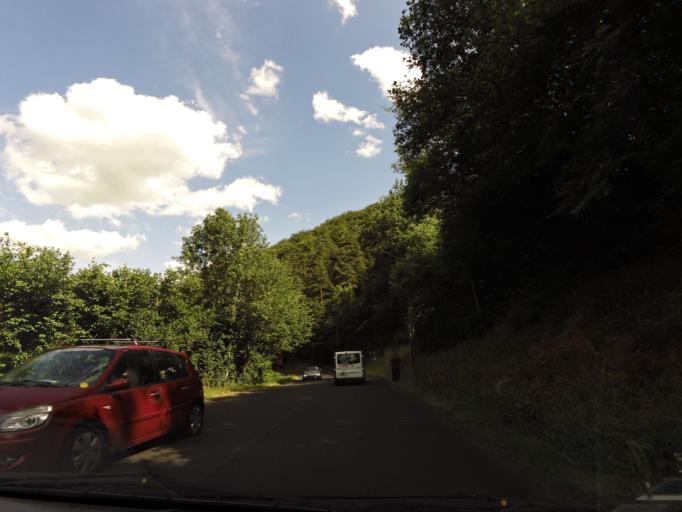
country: FR
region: Auvergne
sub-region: Departement du Puy-de-Dome
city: Aydat
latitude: 45.5758
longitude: 2.9339
